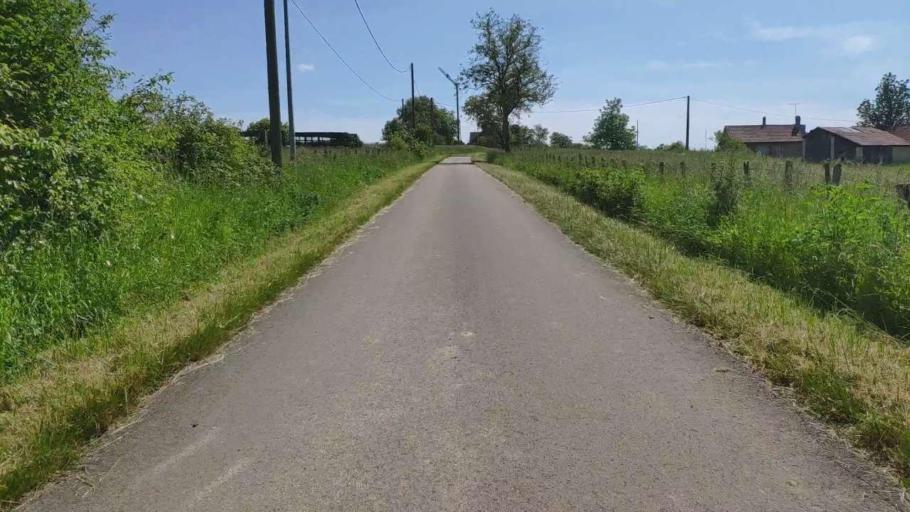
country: FR
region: Franche-Comte
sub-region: Departement du Jura
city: Bletterans
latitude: 46.7927
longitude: 5.4152
